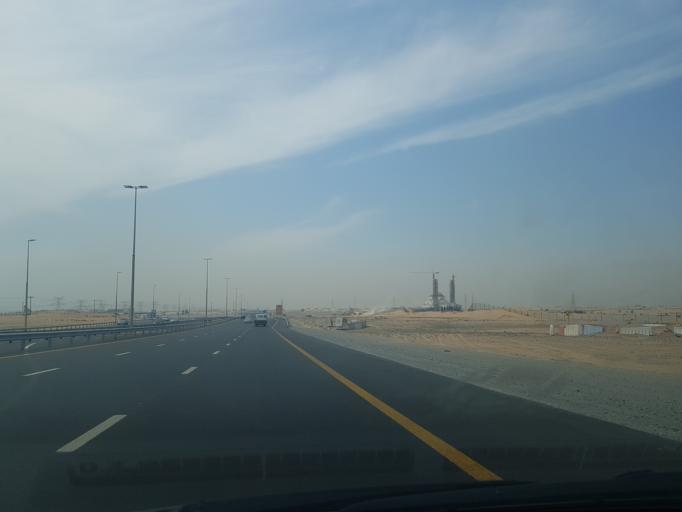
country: AE
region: Ash Shariqah
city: Sharjah
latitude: 25.2333
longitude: 55.5795
